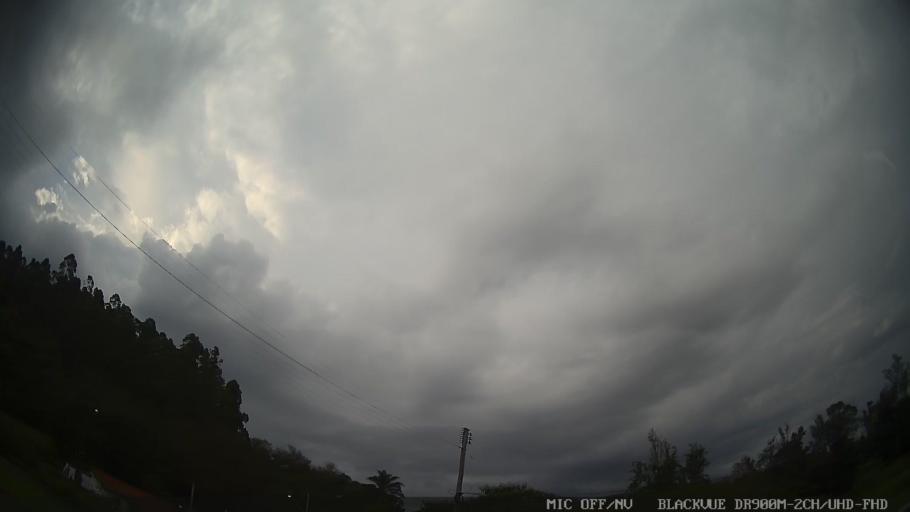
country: BR
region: Sao Paulo
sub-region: Itatiba
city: Itatiba
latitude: -23.0503
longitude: -46.8770
